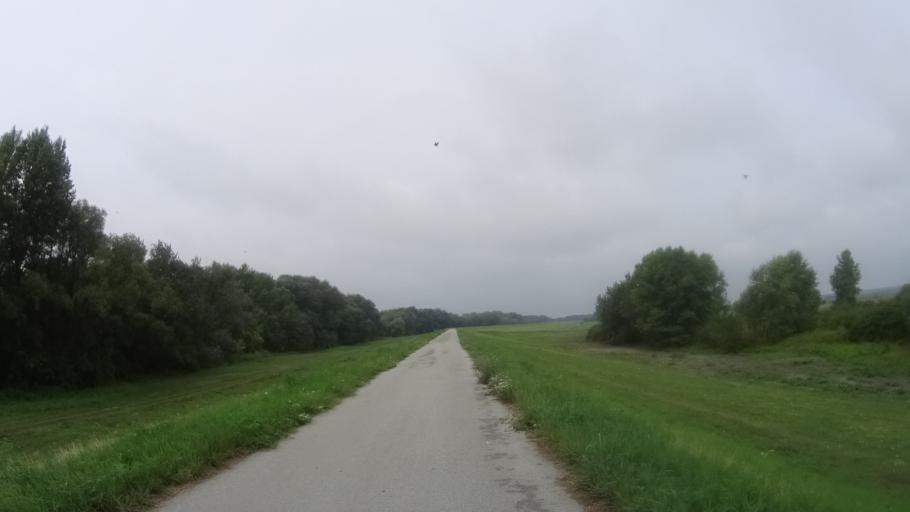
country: HU
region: Komarom-Esztergom
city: Almasfuzito
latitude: 47.7431
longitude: 18.1939
